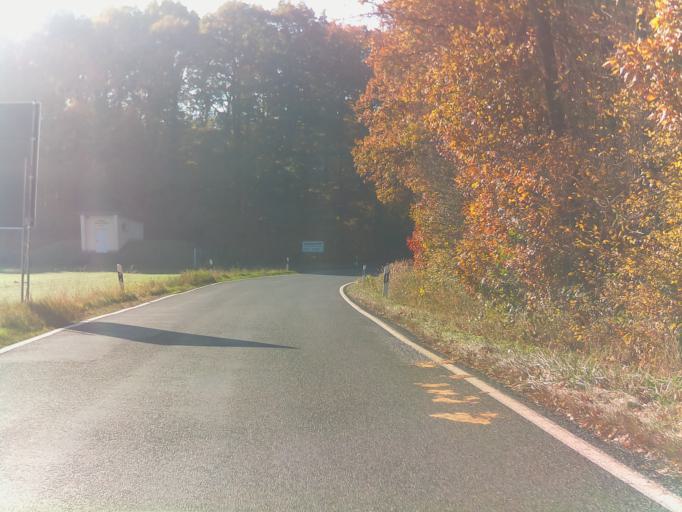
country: DE
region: Bavaria
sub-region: Upper Franconia
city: Burgwindheim
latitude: 49.8764
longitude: 10.5535
